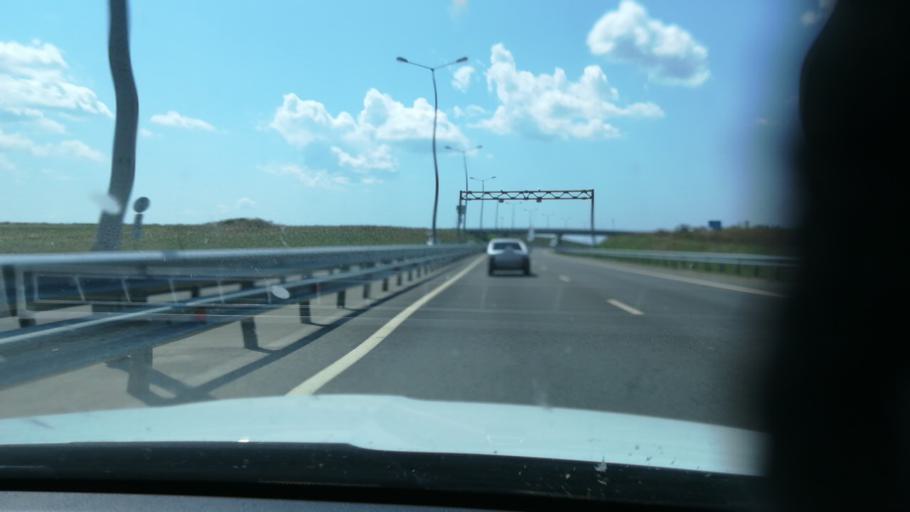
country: RU
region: Krasnodarskiy
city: Vyshestebliyevskaya
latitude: 45.2389
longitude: 37.0534
